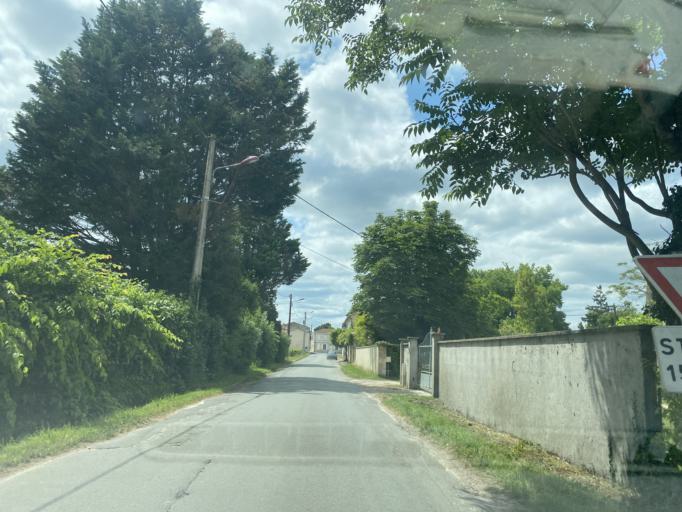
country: FR
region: Aquitaine
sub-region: Departement de la Gironde
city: Soussans
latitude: 45.0569
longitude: -0.6969
